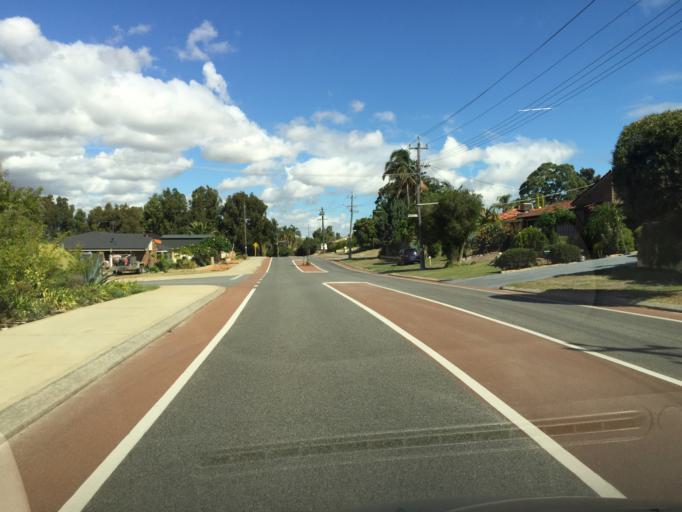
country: AU
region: Western Australia
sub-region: Canning
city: Willetton
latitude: -32.0597
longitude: 115.8933
